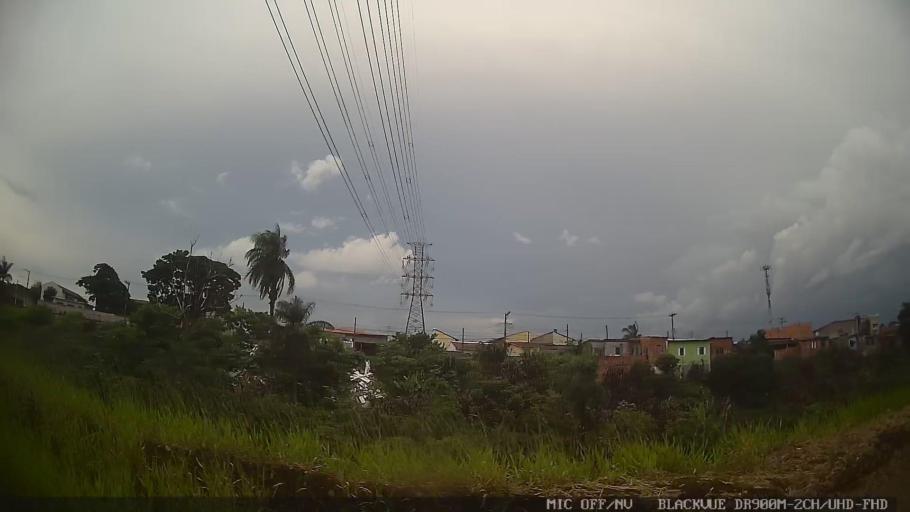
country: BR
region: Sao Paulo
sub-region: Suzano
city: Suzano
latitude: -23.5436
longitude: -46.2886
